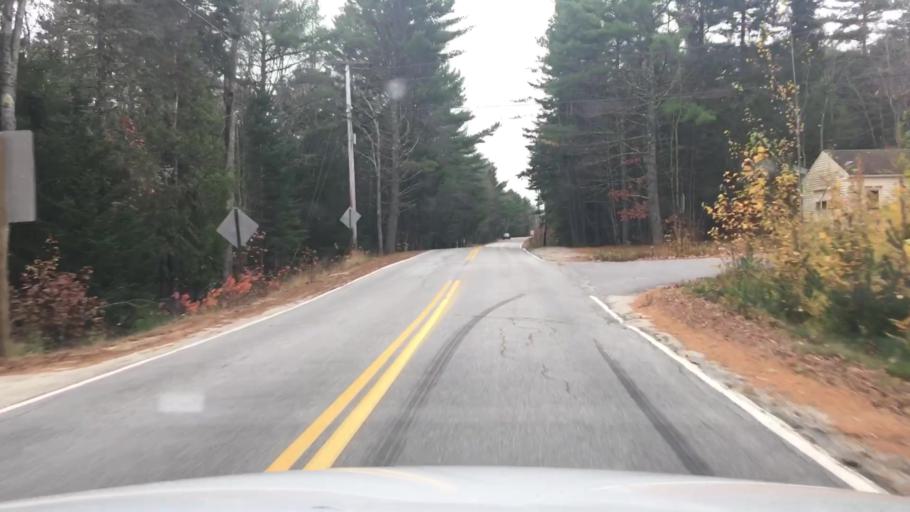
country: US
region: Maine
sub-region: Hancock County
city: Sedgwick
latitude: 44.3230
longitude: -68.5709
